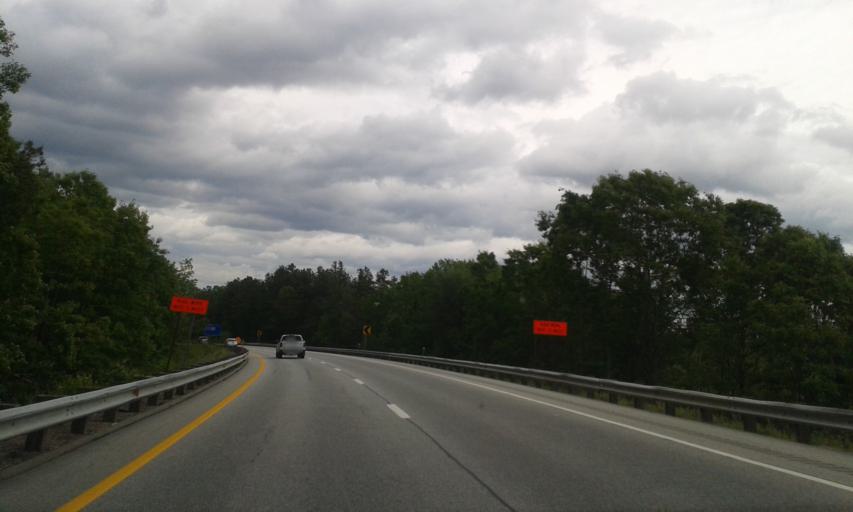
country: US
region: New Hampshire
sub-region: Merrimack County
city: Boscawen
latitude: 43.3392
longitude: -71.6161
